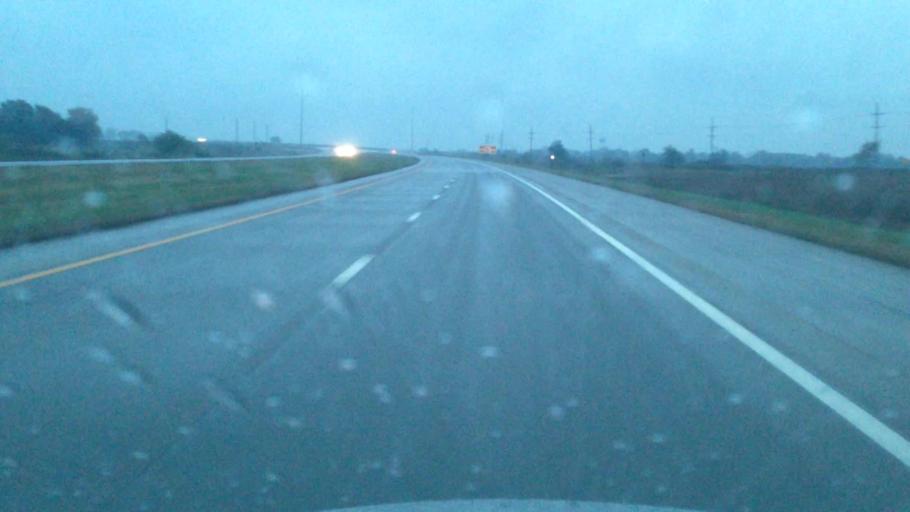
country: US
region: Kansas
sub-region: Franklin County
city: Ottawa
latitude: 38.6970
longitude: -95.2684
